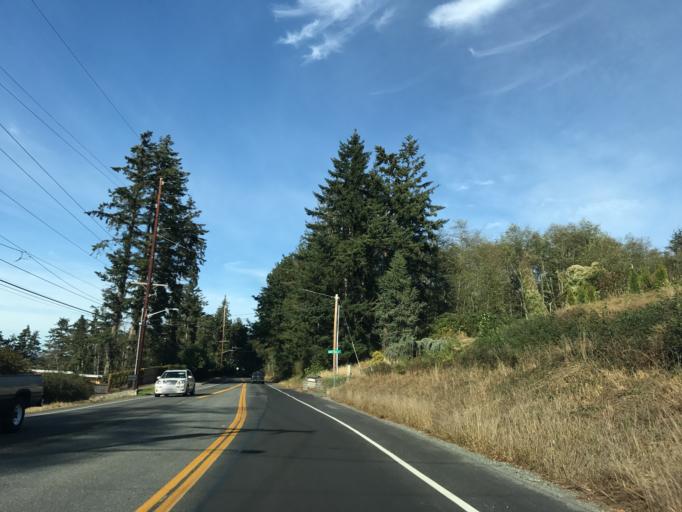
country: US
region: Washington
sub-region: Skagit County
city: Anacortes
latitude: 48.5042
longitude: -122.6627
